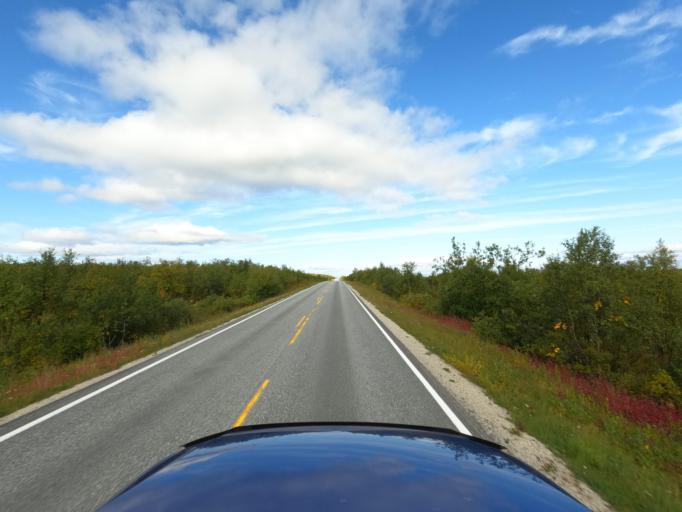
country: NO
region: Finnmark Fylke
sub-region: Karasjok
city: Karasjohka
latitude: 69.6466
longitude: 25.2809
